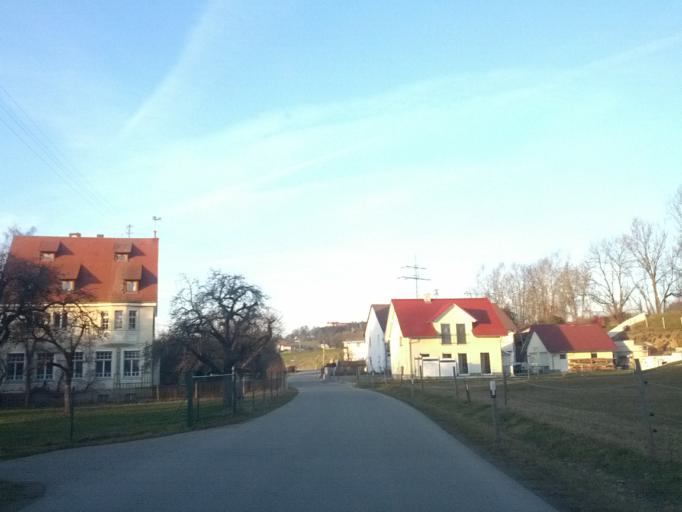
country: DE
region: Bavaria
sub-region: Swabia
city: Kronburg
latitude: 47.8879
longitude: 10.1615
